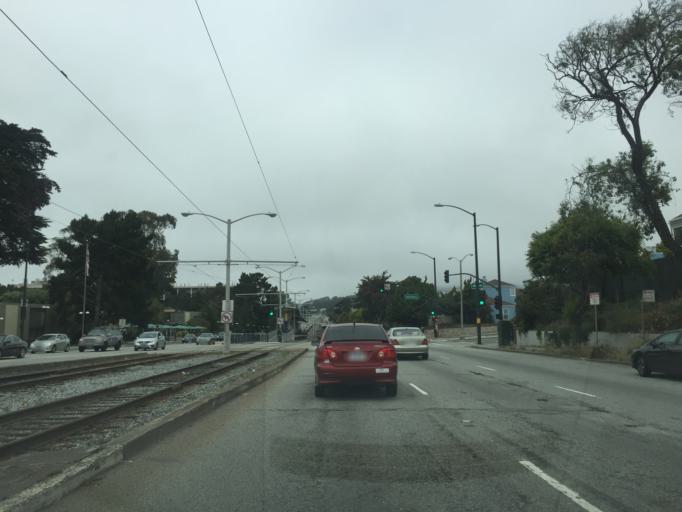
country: US
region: California
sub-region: San Mateo County
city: Daly City
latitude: 37.7205
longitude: -122.4752
